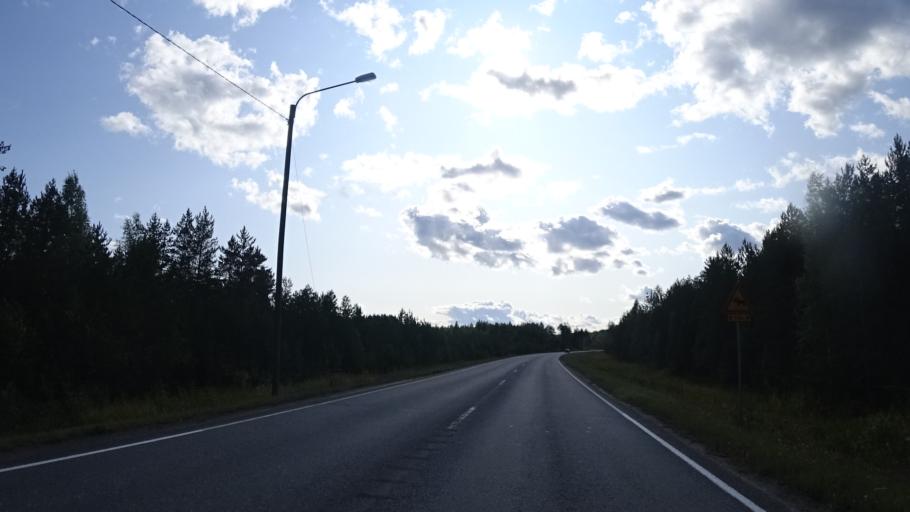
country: FI
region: North Karelia
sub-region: Keski-Karjala
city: Kitee
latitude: 62.0967
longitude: 30.1067
